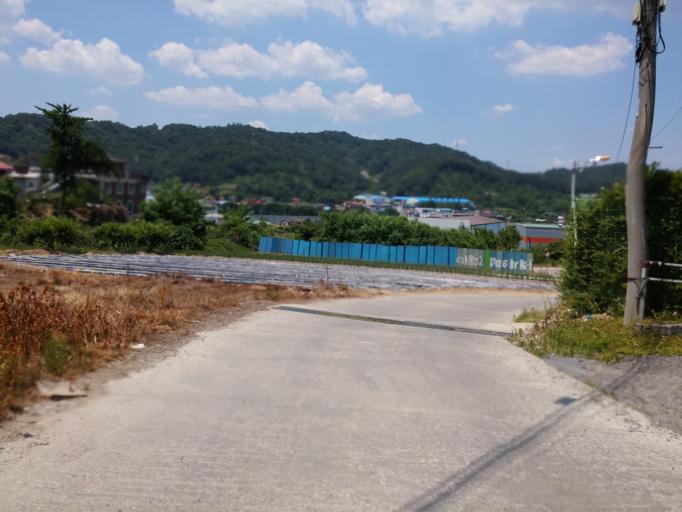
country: KR
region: Chungcheongbuk-do
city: Cheongju-si
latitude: 36.5562
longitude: 127.4372
